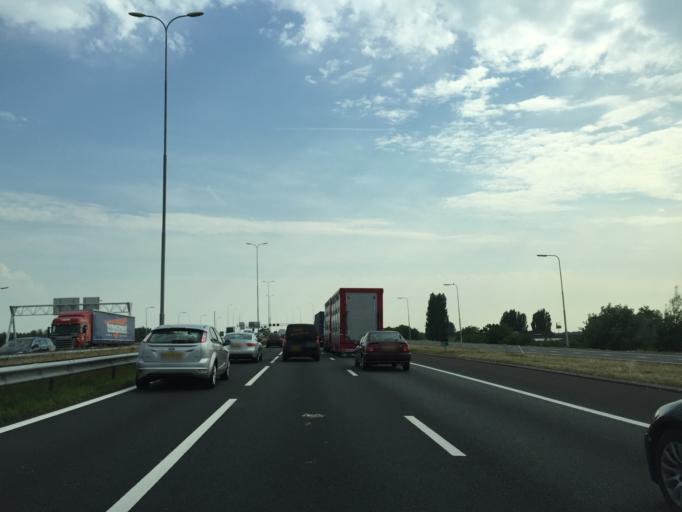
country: NL
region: Utrecht
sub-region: Gemeente Vianen
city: Vianen
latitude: 52.0103
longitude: 5.1183
